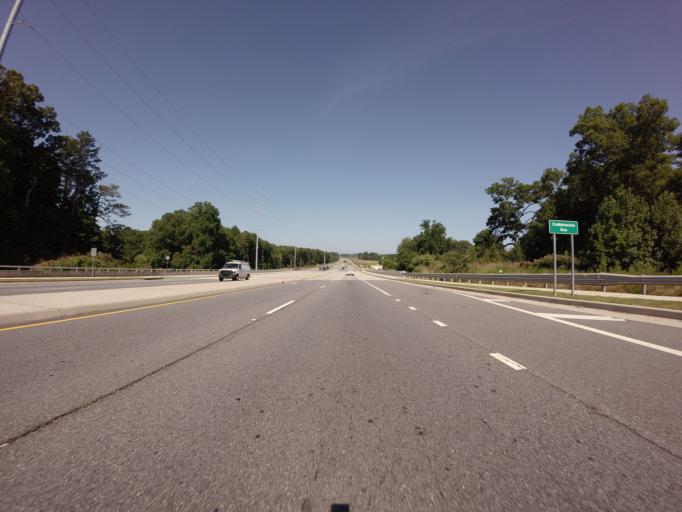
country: US
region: Georgia
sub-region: Gwinnett County
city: Suwanee
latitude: 34.0507
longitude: -84.0968
